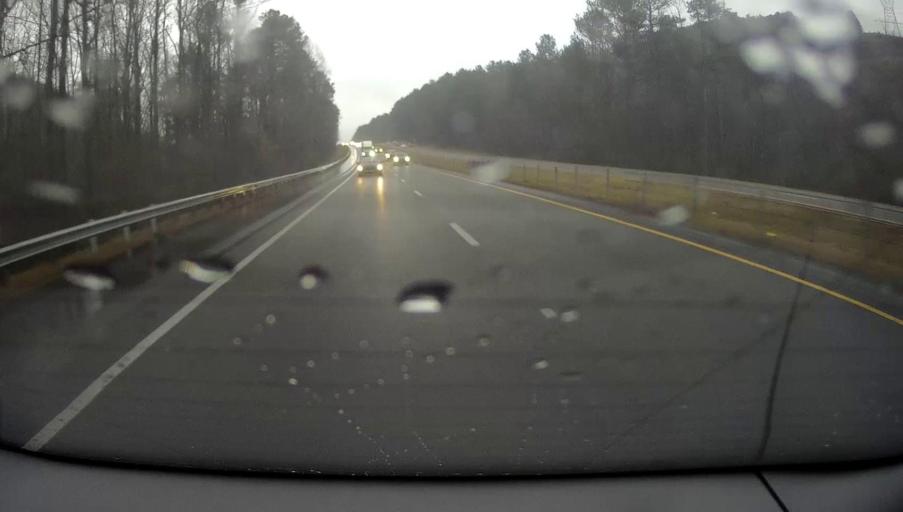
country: US
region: Alabama
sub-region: Cullman County
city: Good Hope
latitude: 34.0109
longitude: -86.8646
